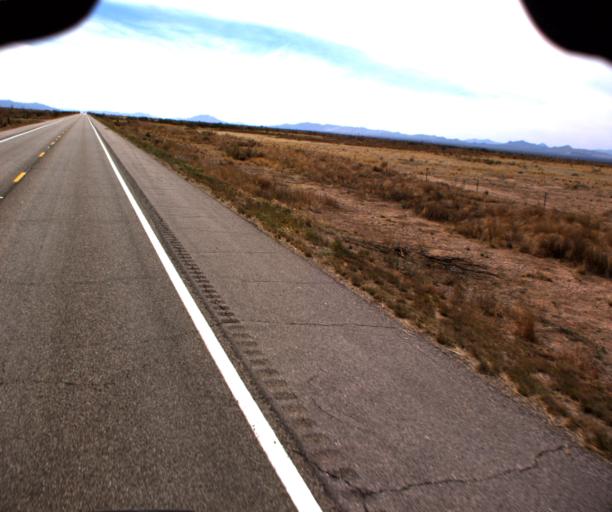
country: US
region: Arizona
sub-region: Cochise County
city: Pirtleville
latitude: 31.5510
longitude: -109.6624
